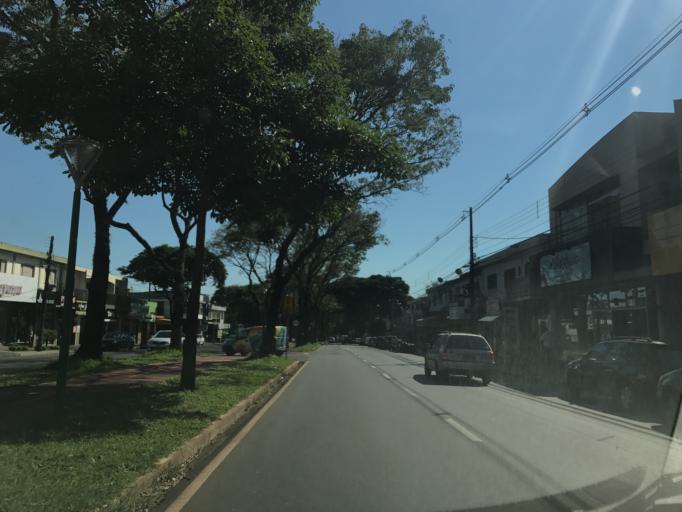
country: BR
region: Parana
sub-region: Maringa
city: Maringa
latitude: -23.4128
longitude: -51.9552
